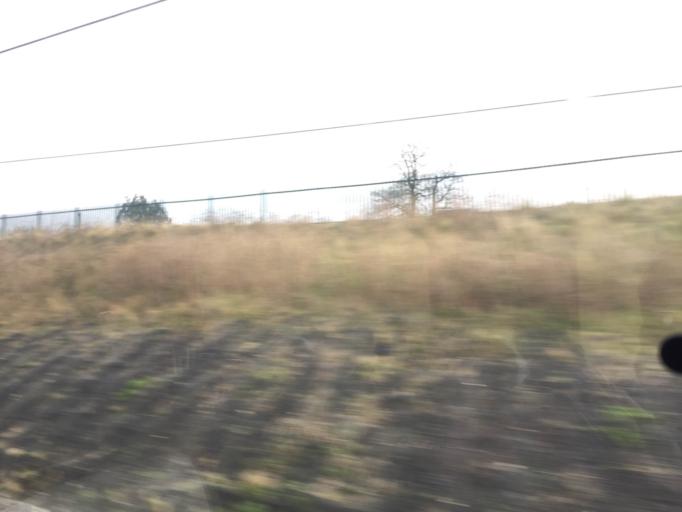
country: GB
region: England
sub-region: Lancashire
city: Galgate
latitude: 53.9796
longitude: -2.7821
